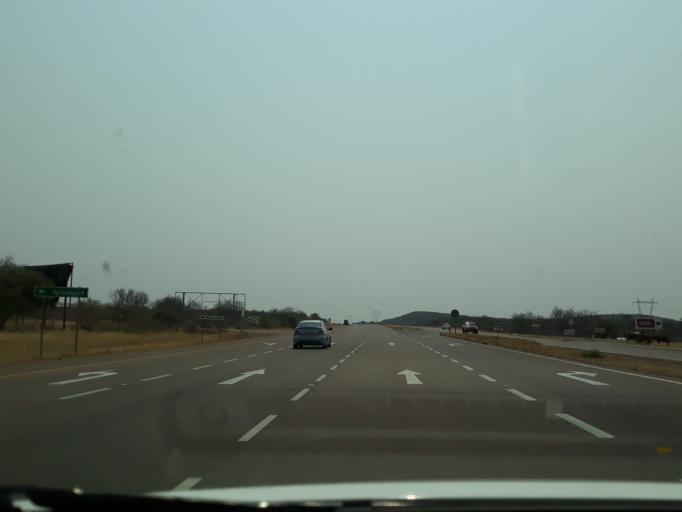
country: BW
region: Kgatleng
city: Bokaa
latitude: -24.4032
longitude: 26.0555
